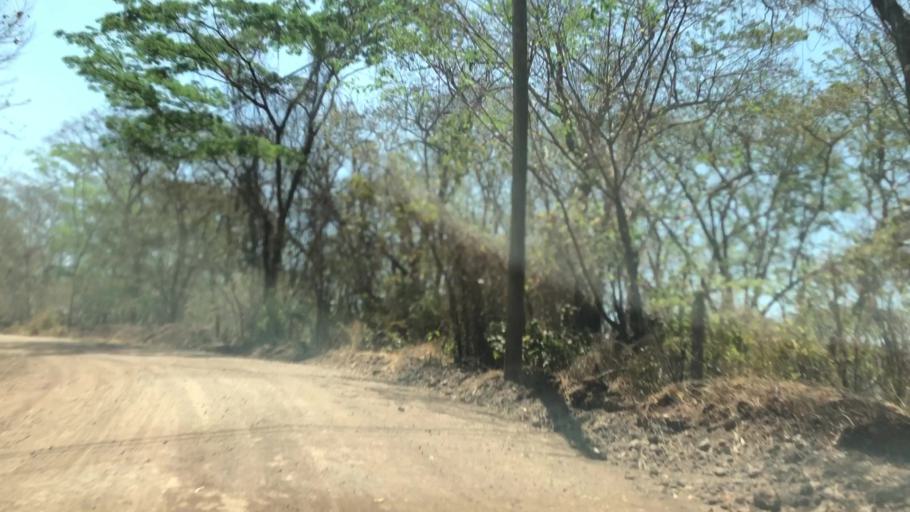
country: CR
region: Guanacaste
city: Sardinal
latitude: 10.3402
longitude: -85.8478
